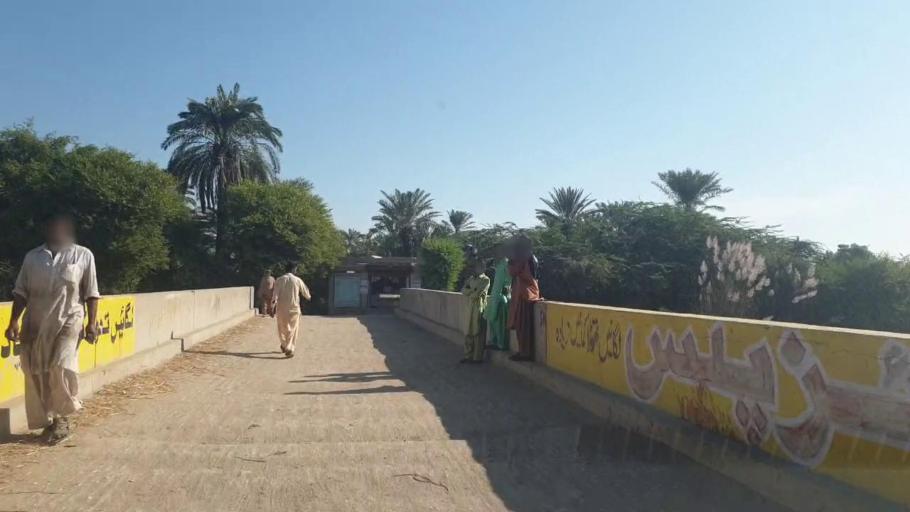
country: PK
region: Sindh
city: Rajo Khanani
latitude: 24.9724
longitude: 68.7661
